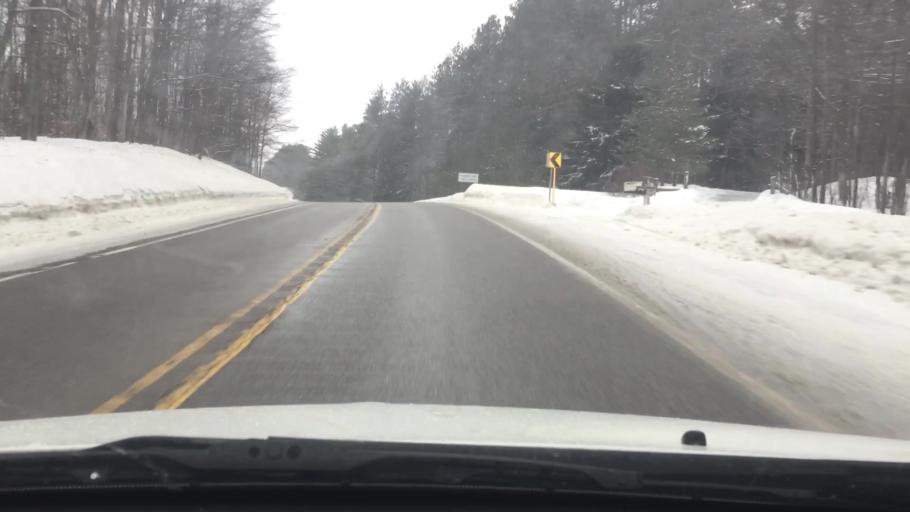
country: US
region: Michigan
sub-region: Otsego County
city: Gaylord
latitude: 45.0616
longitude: -84.8009
